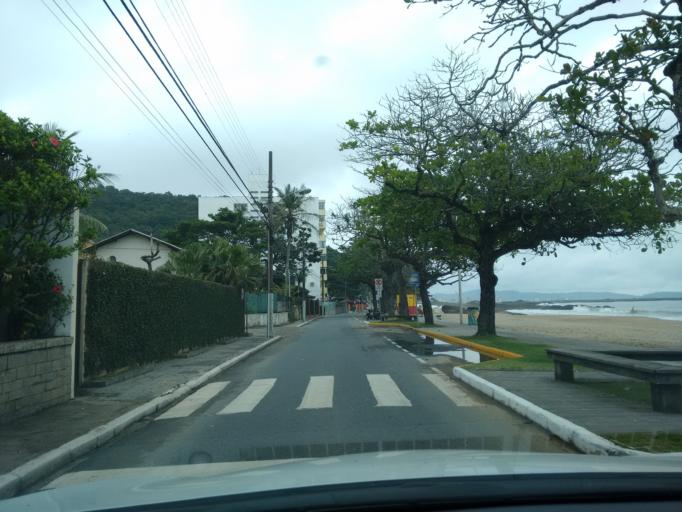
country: BR
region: Santa Catarina
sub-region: Itajai
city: Itajai
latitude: -26.9266
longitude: -48.6339
